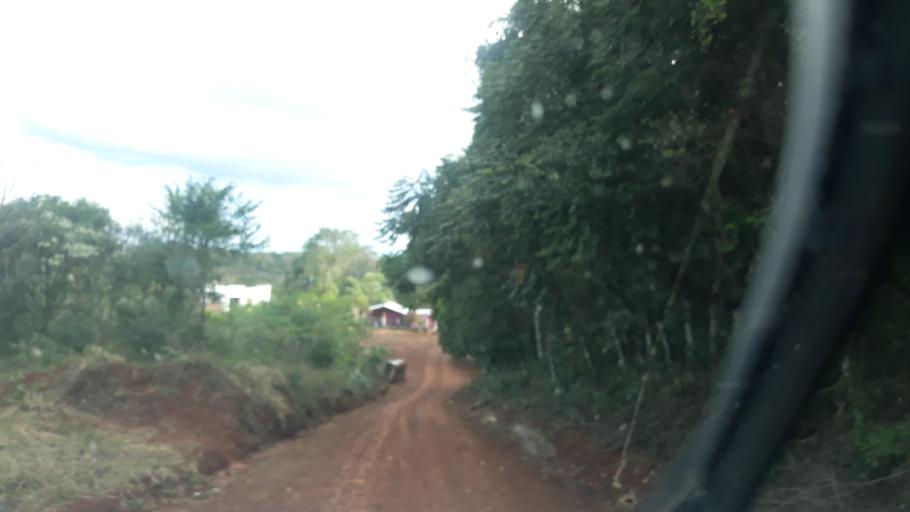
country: AR
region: Misiones
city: Bernardo de Irigoyen
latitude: -26.2675
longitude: -53.6476
